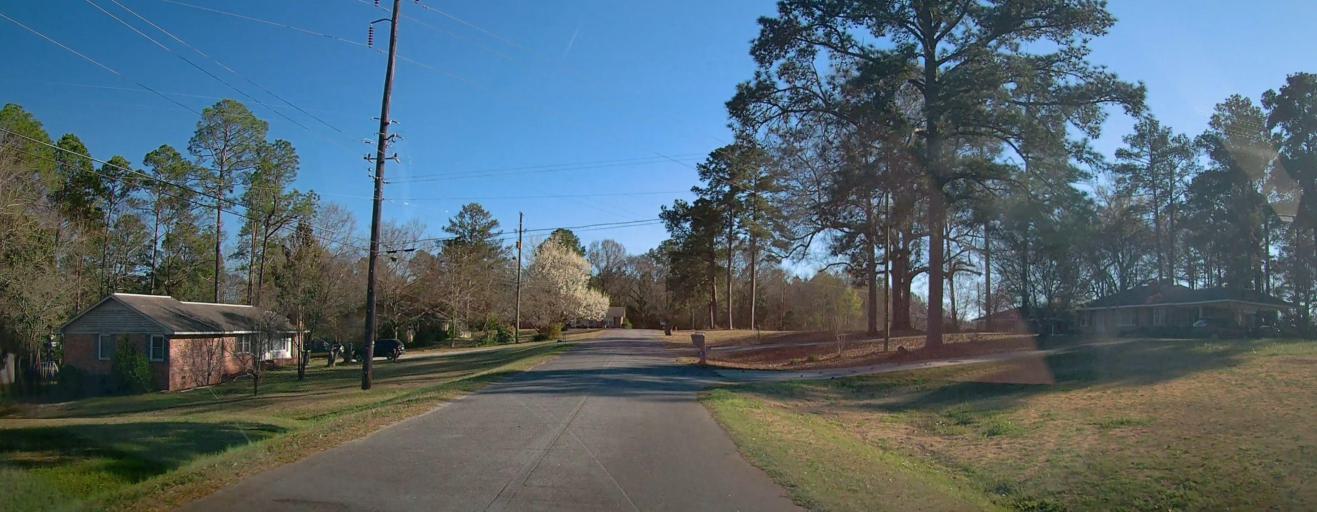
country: US
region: Georgia
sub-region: Taylor County
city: Reynolds
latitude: 32.5524
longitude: -84.0948
